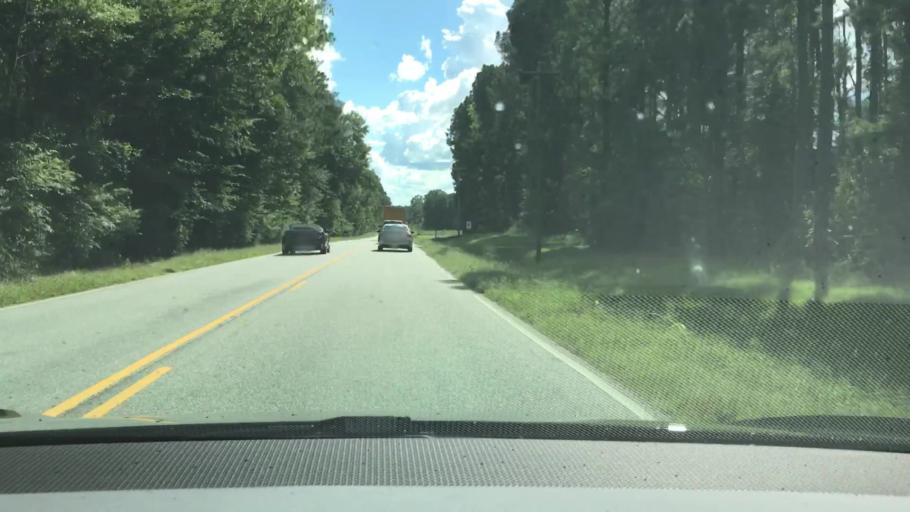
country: US
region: Alabama
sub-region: Montgomery County
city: Pike Road
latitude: 32.2107
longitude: -86.0938
